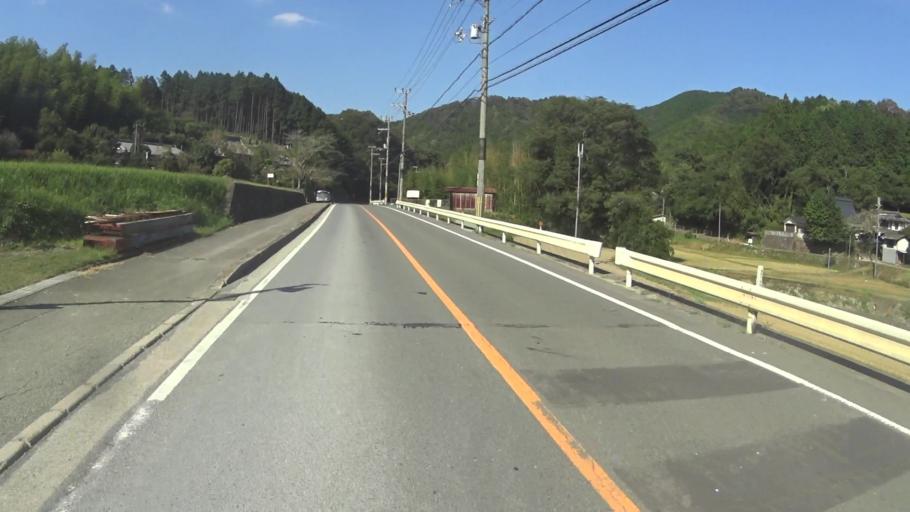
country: JP
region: Kyoto
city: Kameoka
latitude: 34.9351
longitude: 135.5558
